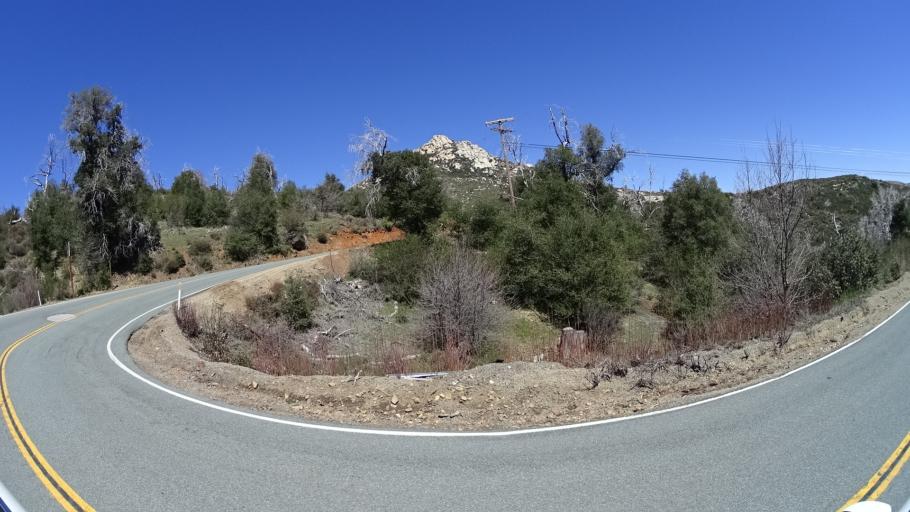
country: US
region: California
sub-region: San Diego County
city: Descanso
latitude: 32.9531
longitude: -116.5778
